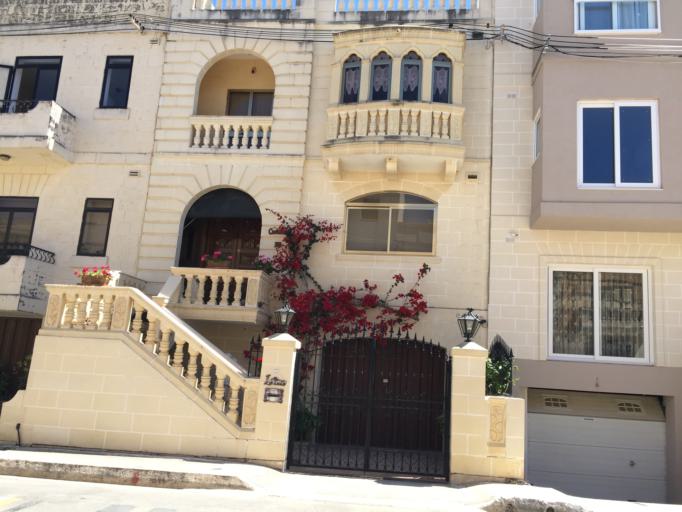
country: MT
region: Saint Julian
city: San Giljan
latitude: 35.9140
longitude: 14.4853
